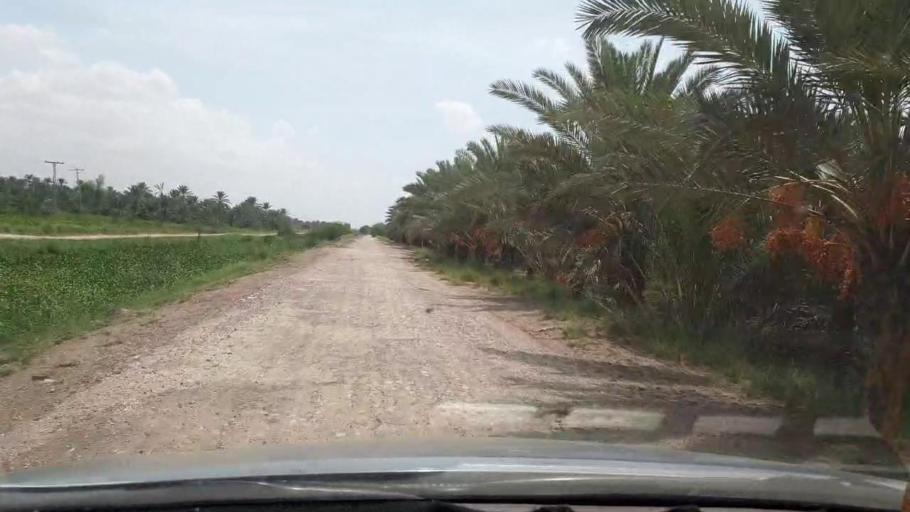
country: PK
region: Sindh
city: Khairpur
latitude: 27.4579
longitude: 68.7910
